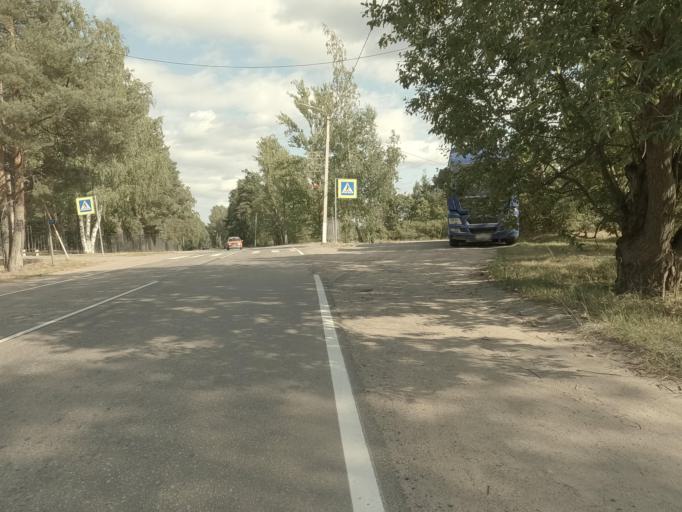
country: RU
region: Leningrad
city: Kamennogorsk
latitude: 60.9476
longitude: 29.1337
